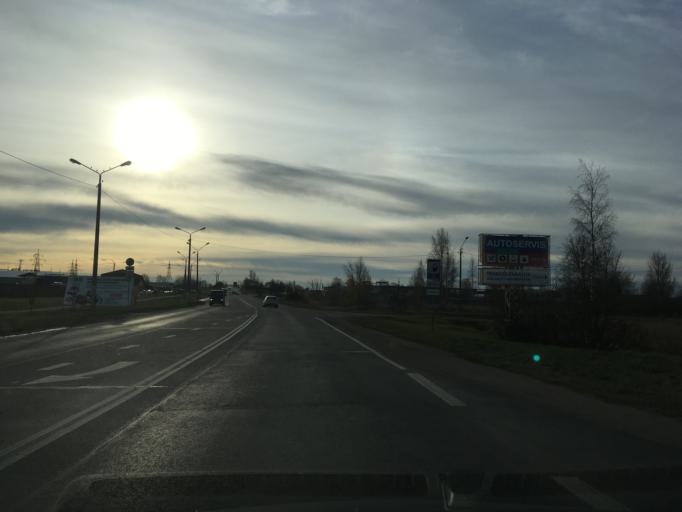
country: EE
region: Ida-Virumaa
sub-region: Narva linn
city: Narva
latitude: 59.3772
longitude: 28.1542
